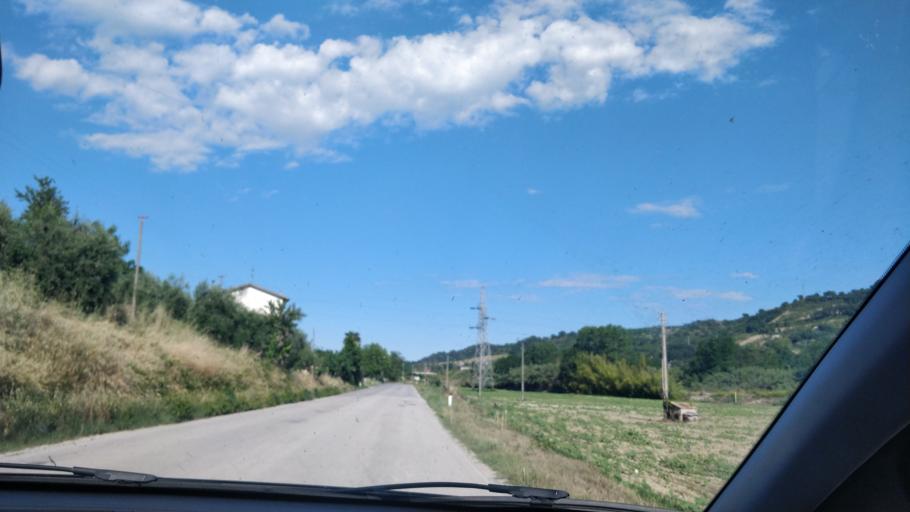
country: IT
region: The Marches
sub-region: Provincia di Ascoli Piceno
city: Massignano
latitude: 43.0376
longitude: 13.8088
